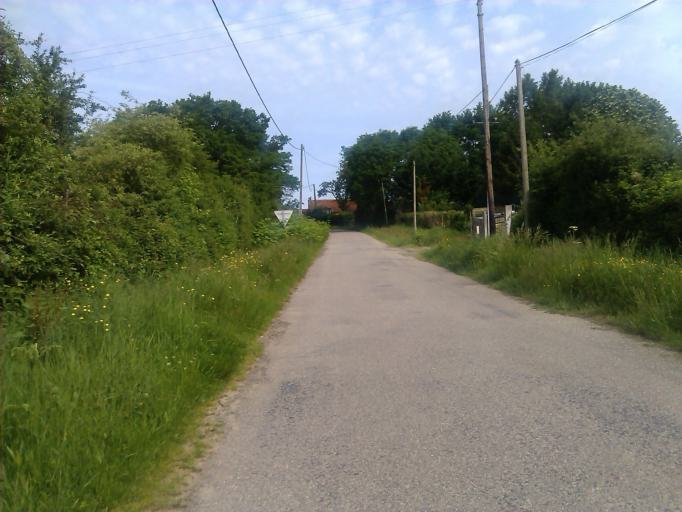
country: FR
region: Auvergne
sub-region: Departement de l'Allier
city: Vallon-en-Sully
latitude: 46.6132
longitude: 2.6571
